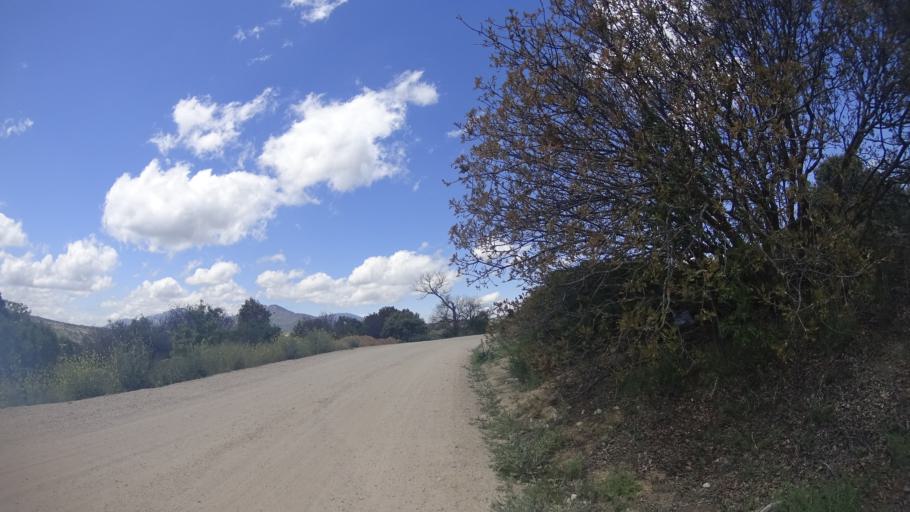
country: ES
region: Madrid
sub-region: Provincia de Madrid
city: San Martin de Valdeiglesias
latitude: 40.3628
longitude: -4.3848
